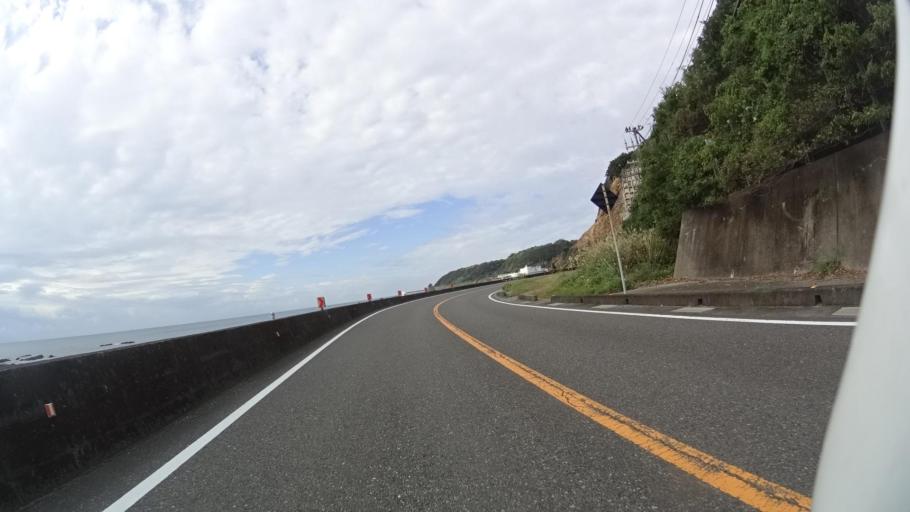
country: JP
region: Wakayama
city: Shingu
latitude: 33.4815
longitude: 135.7521
